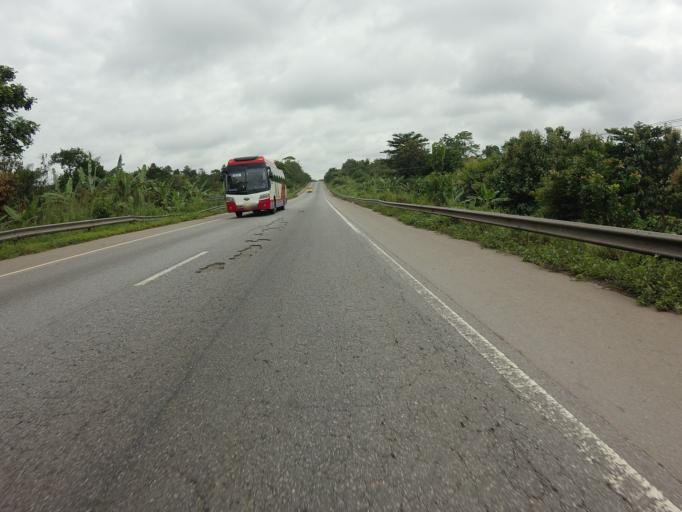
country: GH
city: Bechem
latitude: 7.0758
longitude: -1.7143
